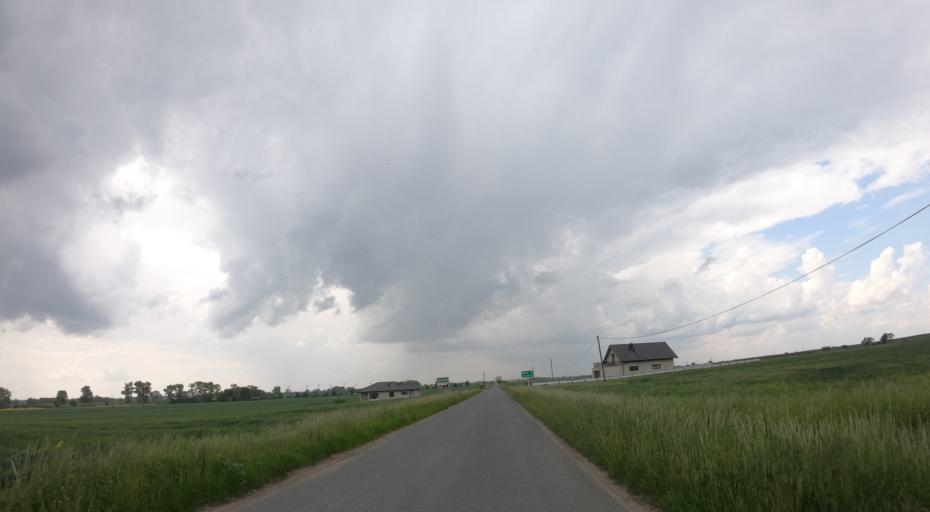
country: PL
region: West Pomeranian Voivodeship
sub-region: Powiat pyrzycki
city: Bielice
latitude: 53.2322
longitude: 14.7622
